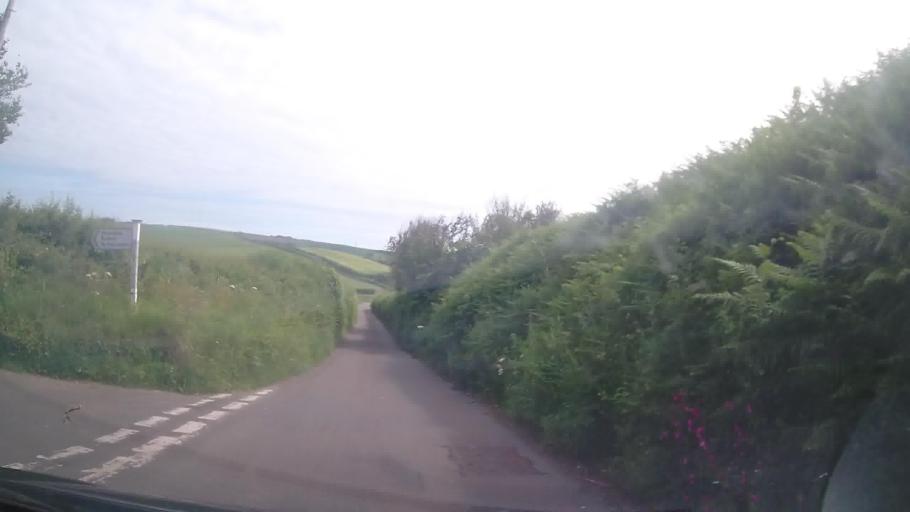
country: GB
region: England
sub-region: Devon
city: Salcombe
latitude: 50.2417
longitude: -3.6791
